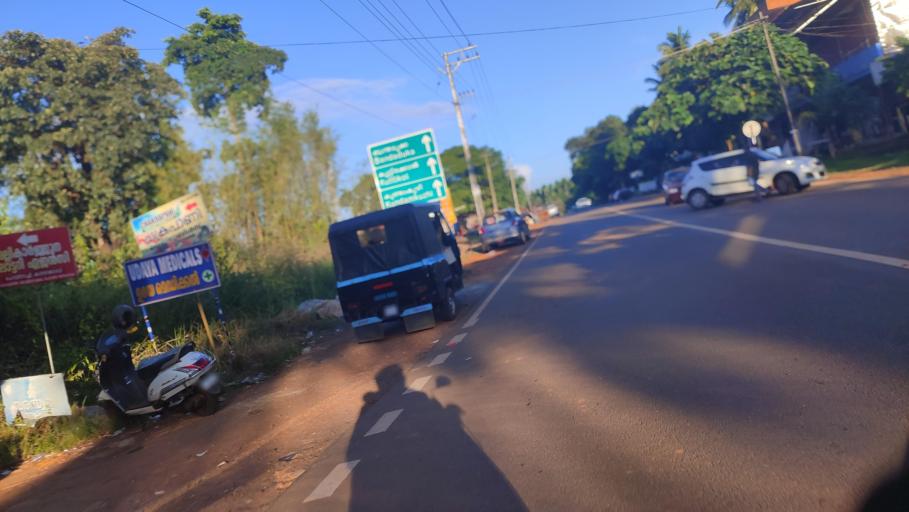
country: IN
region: Kerala
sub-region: Kasaragod District
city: Kasaragod
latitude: 12.4647
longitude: 75.0593
